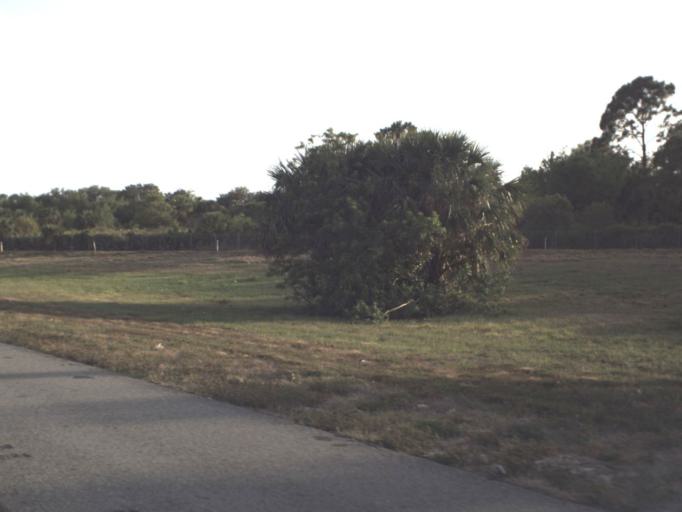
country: US
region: Florida
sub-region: Brevard County
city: Port Saint John
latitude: 28.4505
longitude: -80.8213
